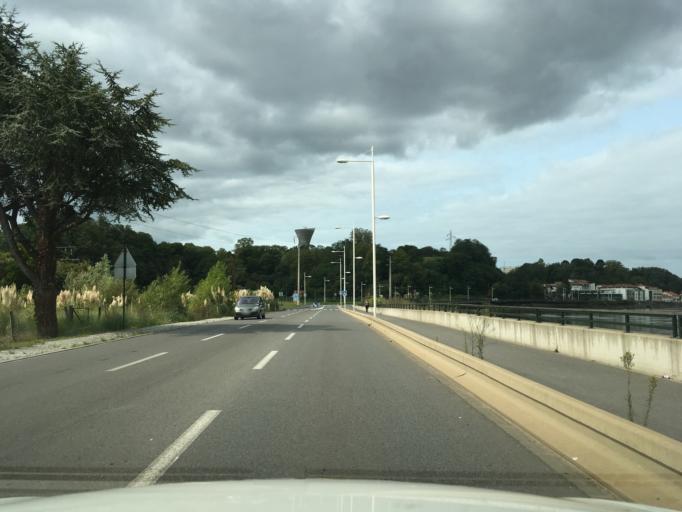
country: FR
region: Aquitaine
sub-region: Departement des Pyrenees-Atlantiques
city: Bayonne
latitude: 43.4839
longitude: -1.4517
